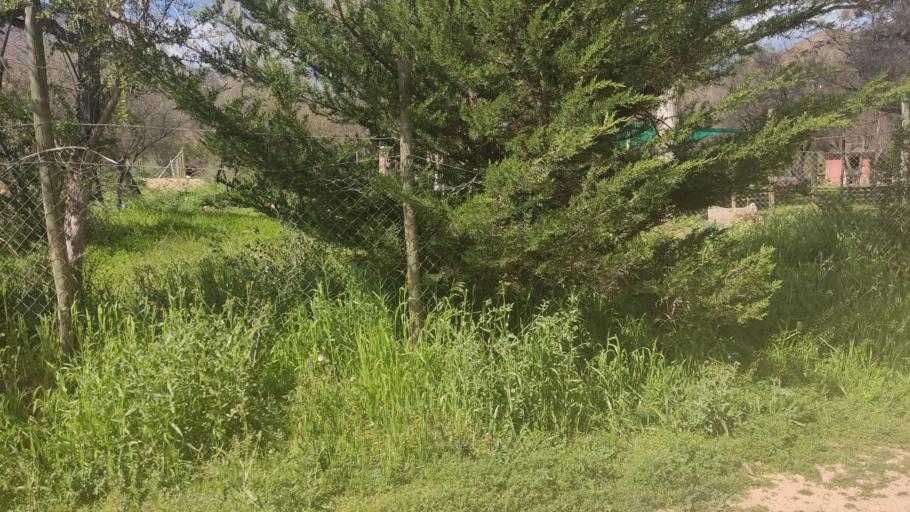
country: CL
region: Valparaiso
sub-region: Provincia de Marga Marga
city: Limache
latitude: -33.1733
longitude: -71.1649
